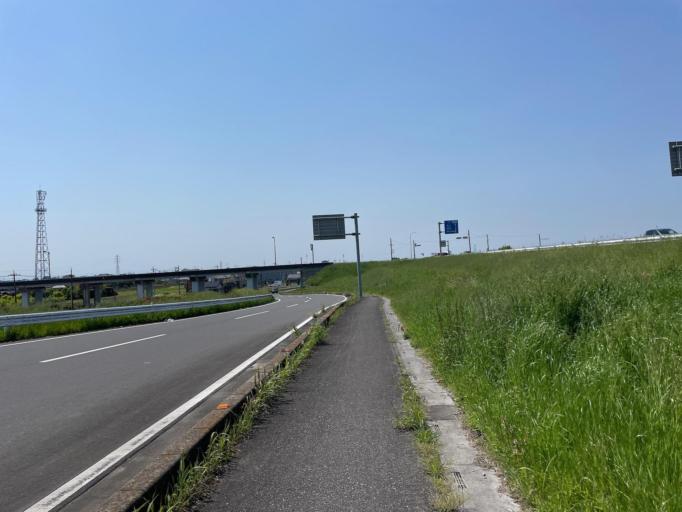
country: JP
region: Ibaraki
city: Koga
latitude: 36.2008
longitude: 139.6787
